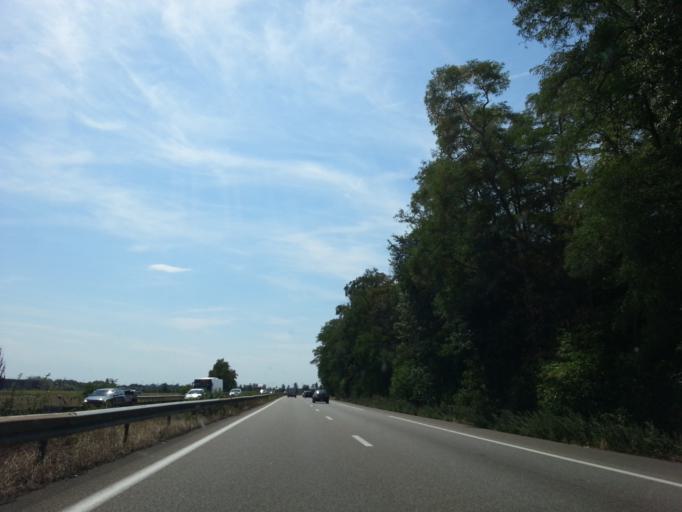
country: FR
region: Alsace
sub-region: Departement du Haut-Rhin
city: Houssen
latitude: 48.1344
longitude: 7.3652
